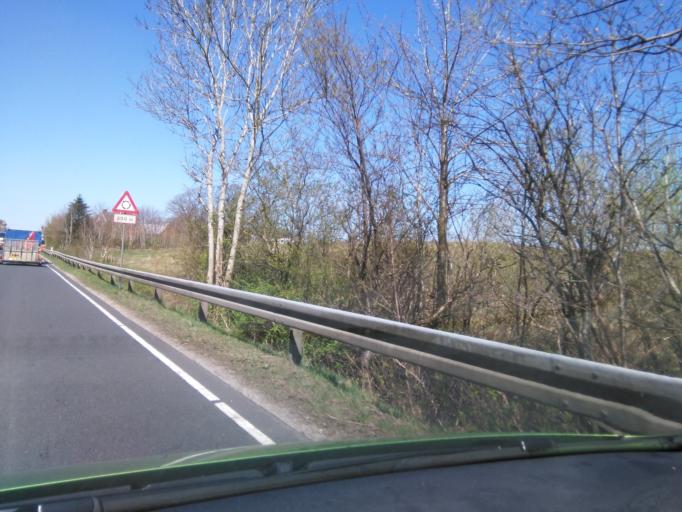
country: DK
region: South Denmark
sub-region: Varde Kommune
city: Olgod
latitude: 55.7074
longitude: 8.7552
